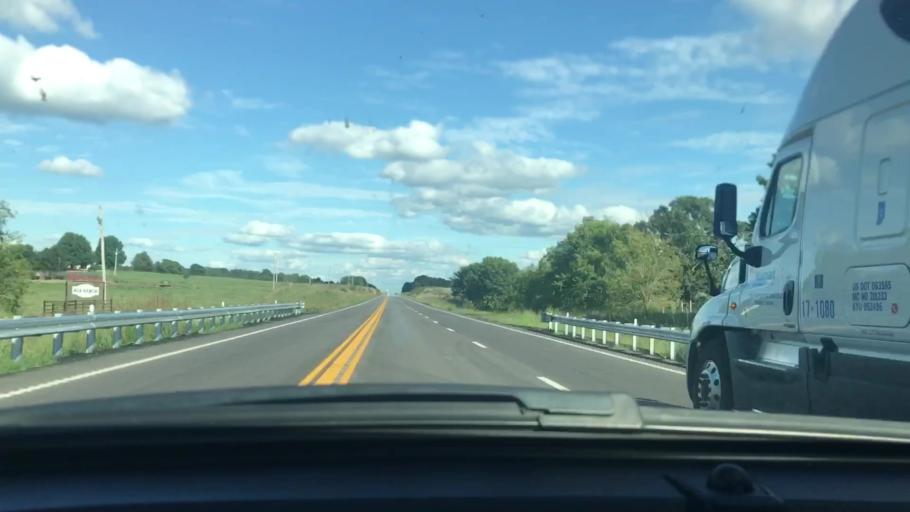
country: US
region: Missouri
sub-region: Oregon County
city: Thayer
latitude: 36.5861
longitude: -91.6251
